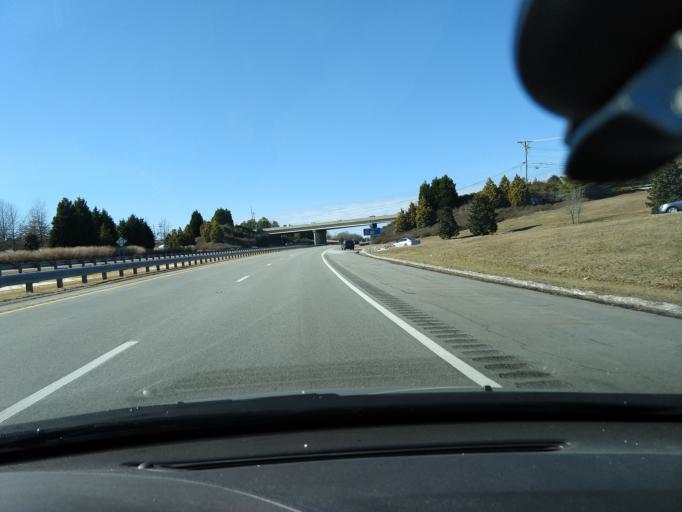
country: US
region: North Carolina
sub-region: Guilford County
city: Greensboro
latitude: 36.1156
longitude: -79.8756
